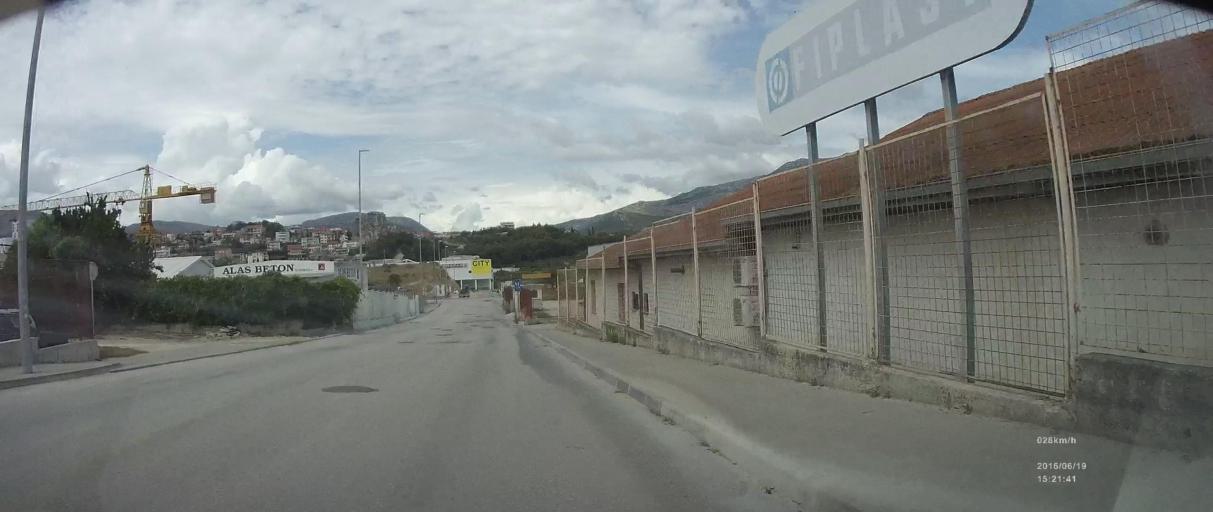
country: HR
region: Splitsko-Dalmatinska
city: Kamen
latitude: 43.5092
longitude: 16.5023
